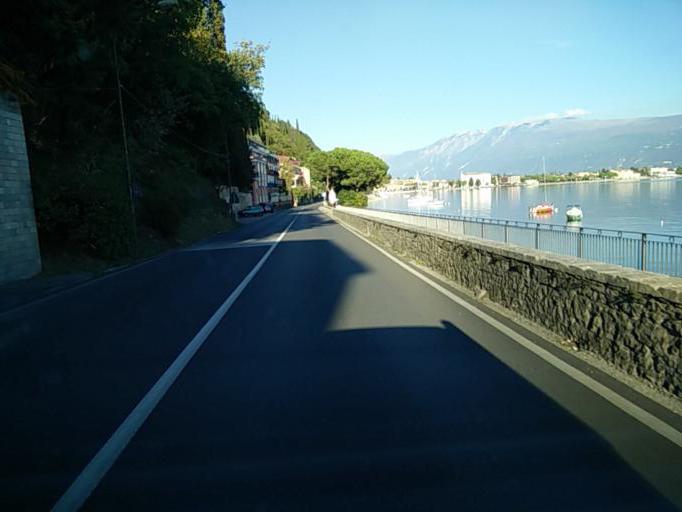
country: IT
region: Lombardy
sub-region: Provincia di Brescia
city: Gardone Riviera
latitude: 45.6304
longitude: 10.5877
